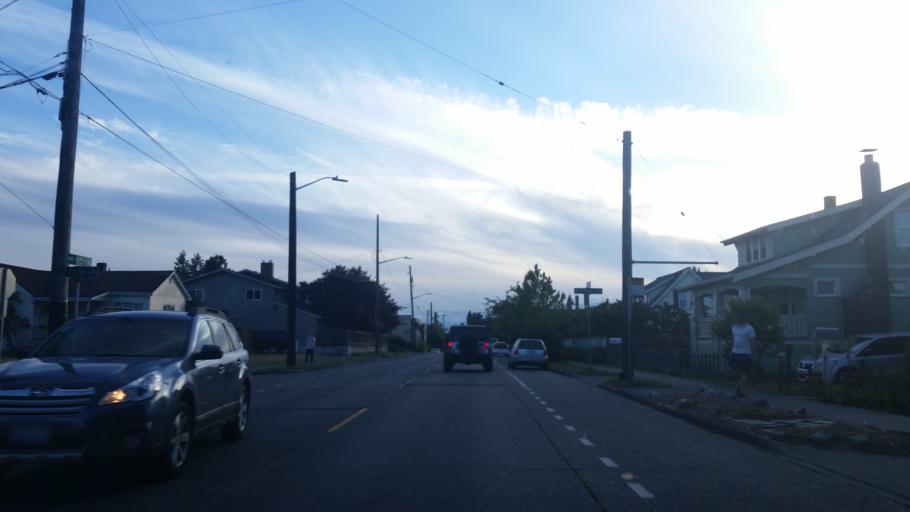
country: US
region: Washington
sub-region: King County
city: Shoreline
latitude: 47.6906
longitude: -122.3904
